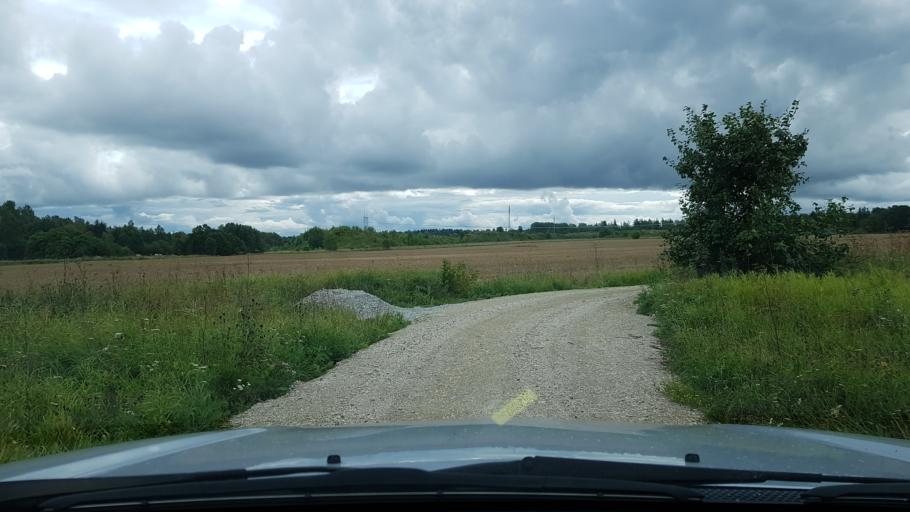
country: EE
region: Harju
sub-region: Rae vald
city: Vaida
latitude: 59.2756
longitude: 25.0294
